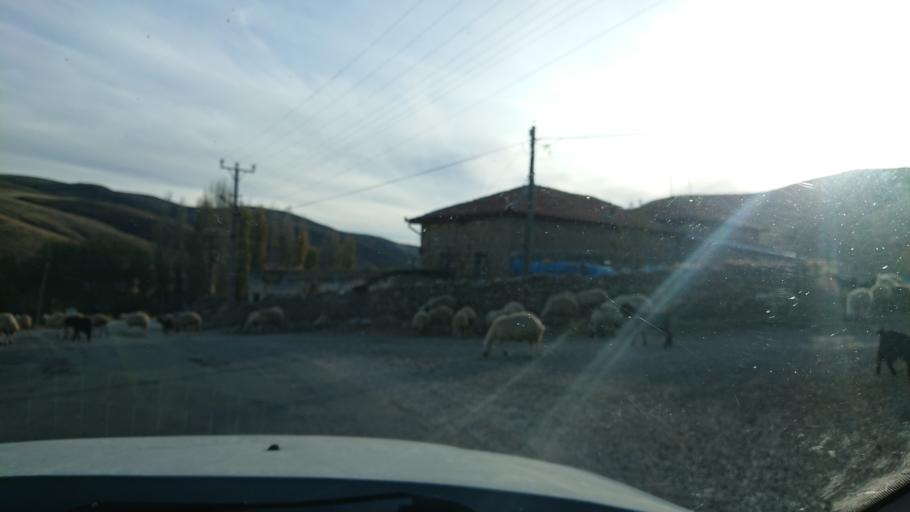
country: TR
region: Ankara
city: Sereflikochisar
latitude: 38.7651
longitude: 33.6991
